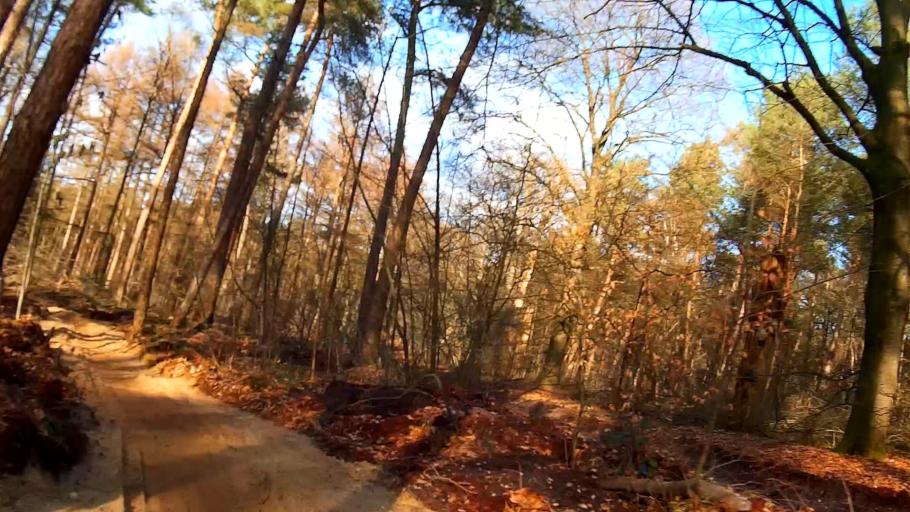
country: NL
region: Utrecht
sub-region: Gemeente Utrechtse Heuvelrug
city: Amerongen
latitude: 52.0174
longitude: 5.4691
